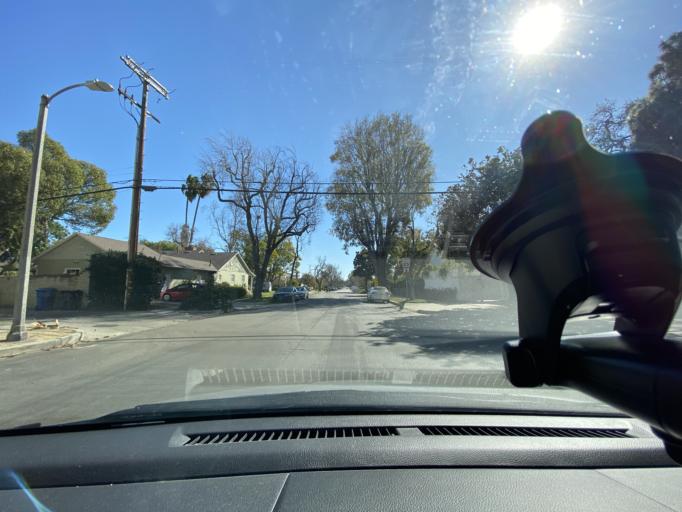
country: US
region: California
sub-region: Los Angeles County
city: Westwood, Los Angeles
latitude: 34.0246
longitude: -118.4339
